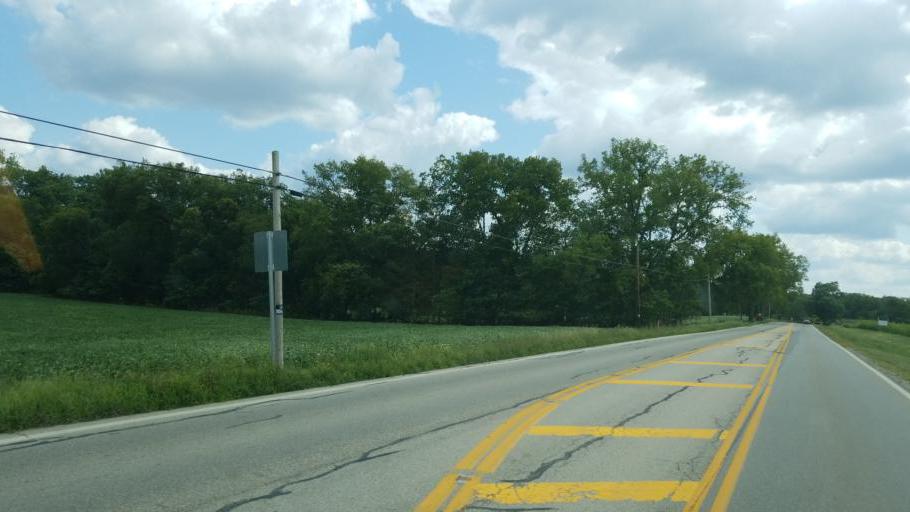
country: US
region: Ohio
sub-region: Delaware County
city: Powell
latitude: 40.1900
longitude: -83.0525
